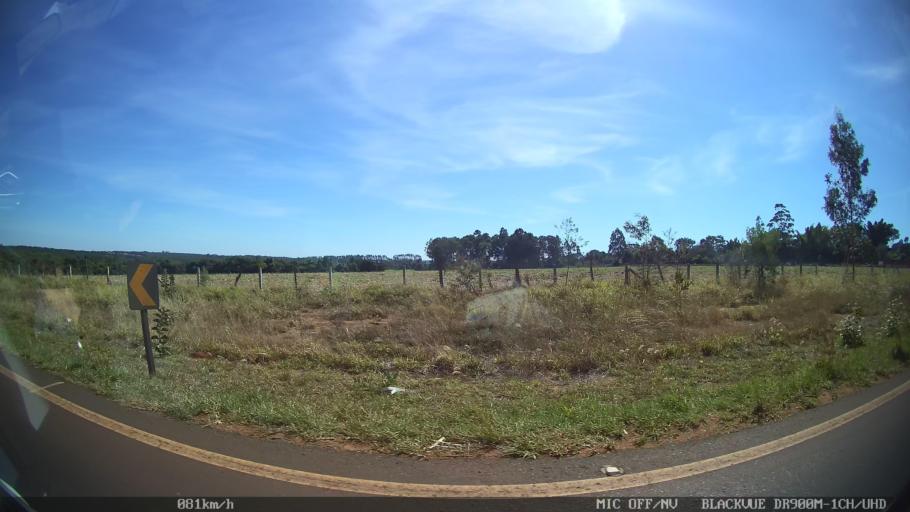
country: BR
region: Sao Paulo
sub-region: Franca
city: Franca
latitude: -20.5569
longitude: -47.4988
